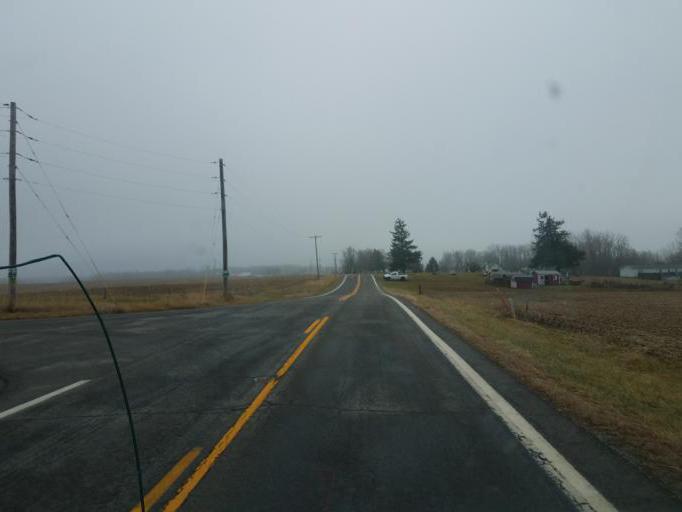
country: US
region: Ohio
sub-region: Champaign County
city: North Lewisburg
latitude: 40.2635
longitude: -83.5885
